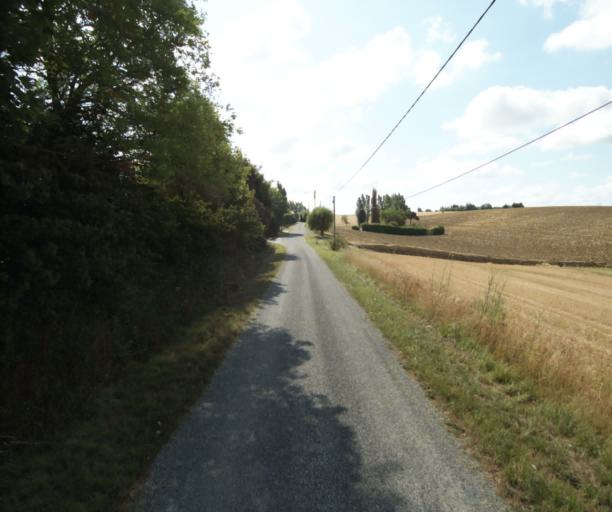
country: FR
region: Midi-Pyrenees
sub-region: Departement de la Haute-Garonne
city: Avignonet-Lauragais
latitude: 43.4352
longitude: 1.7918
